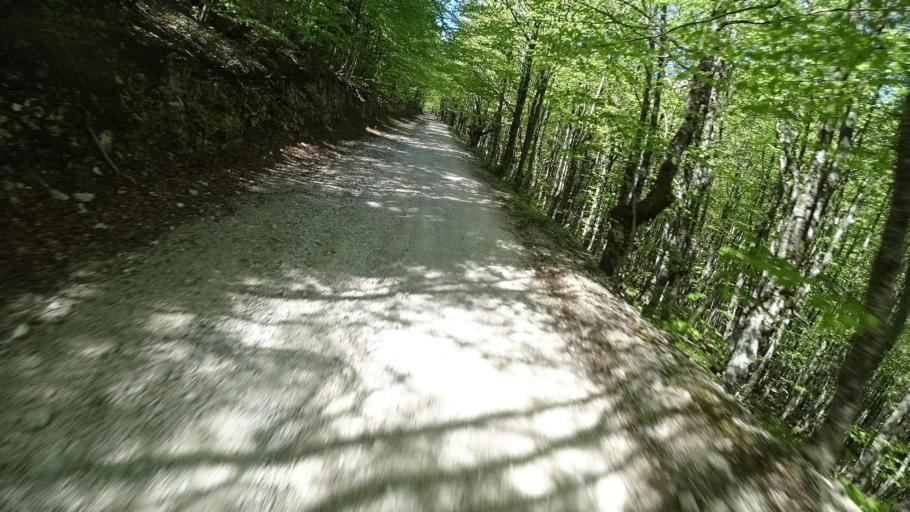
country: BA
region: Federation of Bosnia and Herzegovina
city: Gracanica
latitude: 43.7026
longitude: 18.2786
